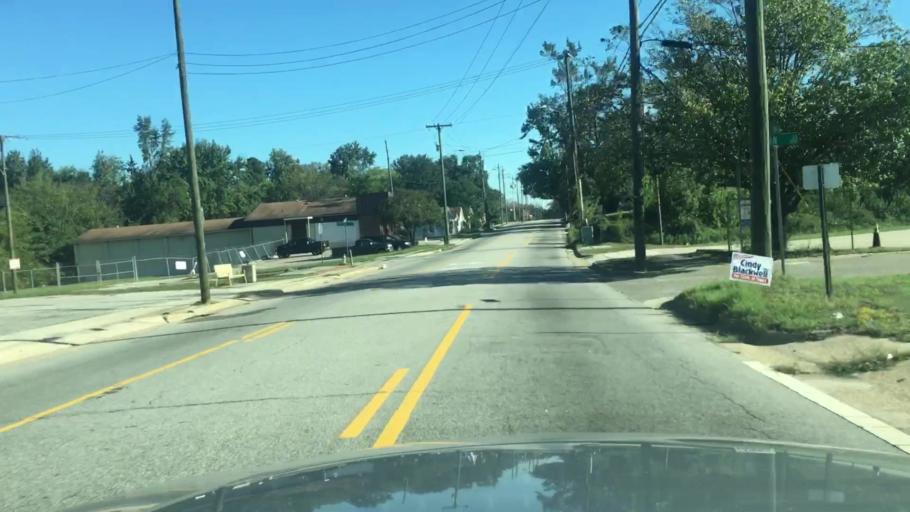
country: US
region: North Carolina
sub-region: Cumberland County
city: Fayetteville
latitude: 35.0322
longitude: -78.8933
